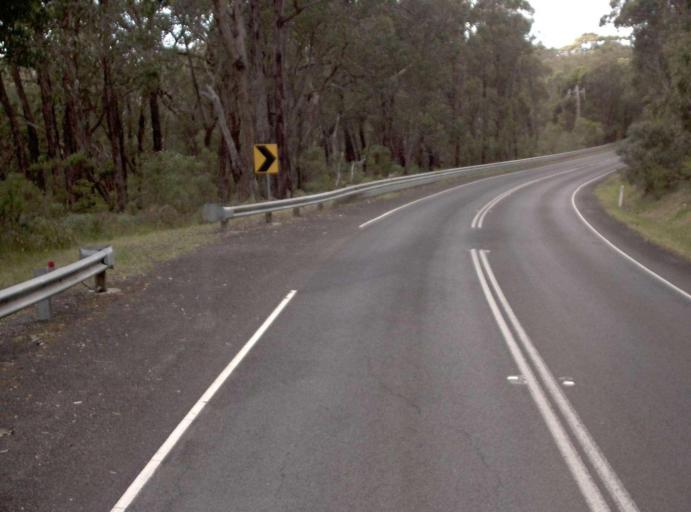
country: AU
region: Victoria
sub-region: Mornington Peninsula
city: Dromana
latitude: -38.3576
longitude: 144.9673
